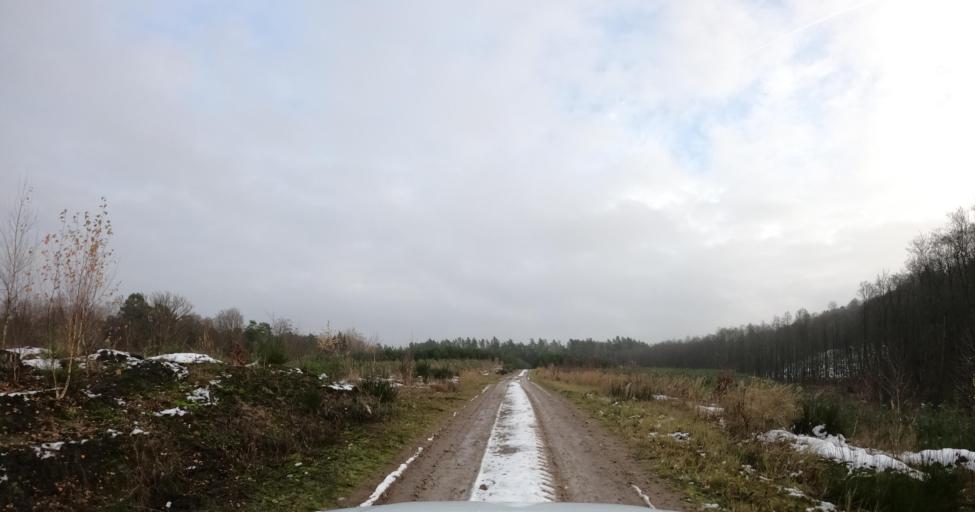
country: PL
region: West Pomeranian Voivodeship
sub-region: Powiat swidwinski
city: Rabino
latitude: 53.9090
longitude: 15.8809
